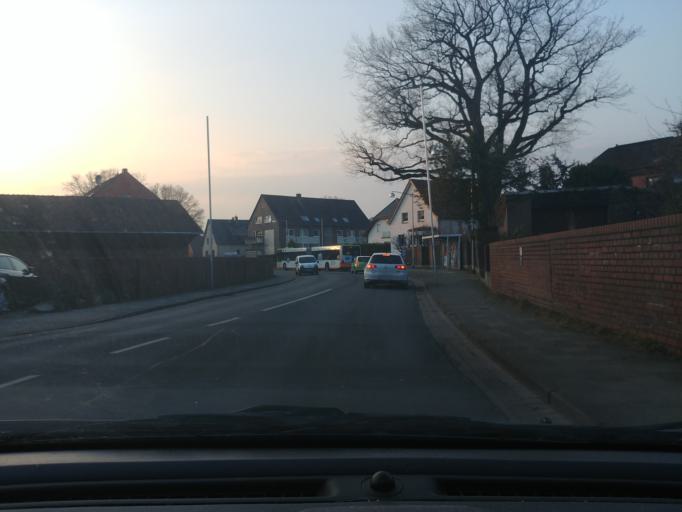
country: DE
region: Lower Saxony
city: Langenhagen
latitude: 52.4389
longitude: 9.7020
